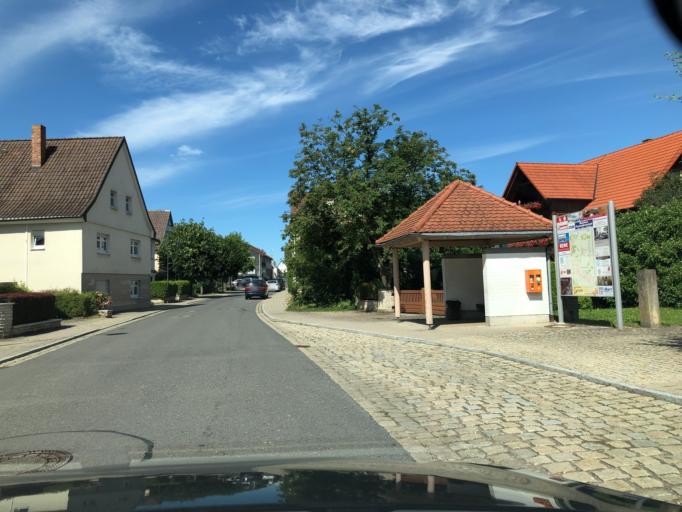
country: DE
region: Bavaria
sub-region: Upper Franconia
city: Sonnefeld
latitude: 50.2166
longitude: 11.0874
